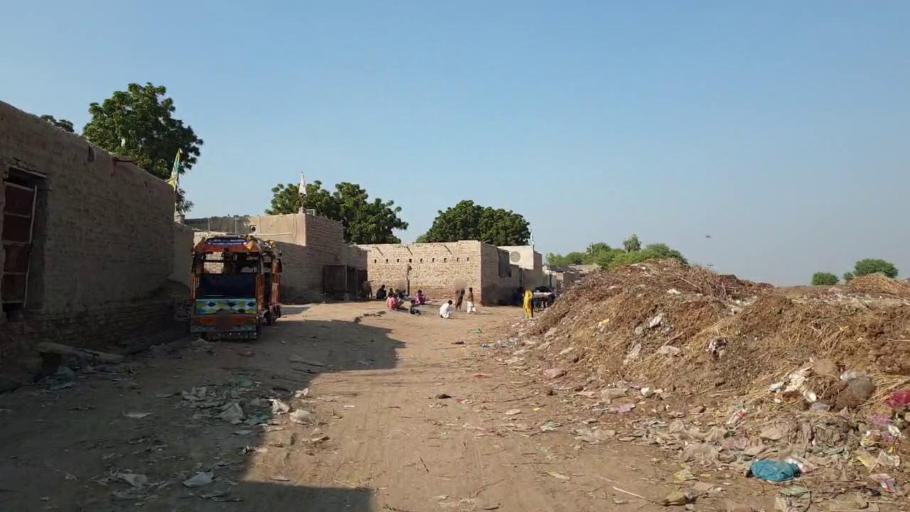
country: PK
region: Sindh
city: Sehwan
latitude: 26.4491
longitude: 67.8175
